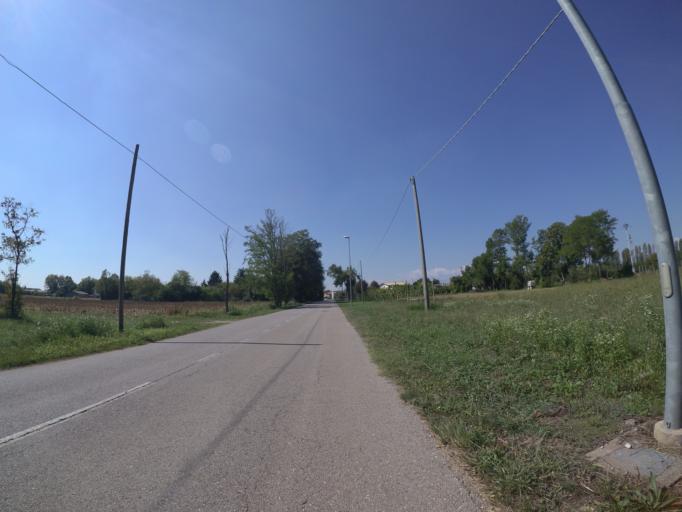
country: IT
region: Friuli Venezia Giulia
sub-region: Provincia di Udine
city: Codroipo
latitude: 45.9776
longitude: 12.9788
